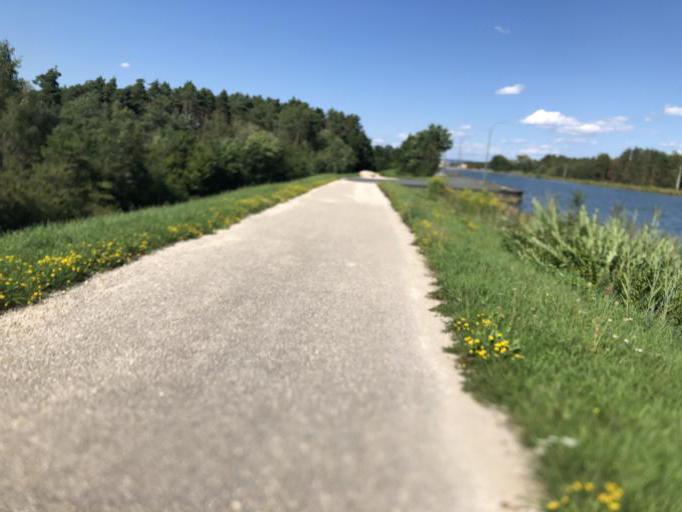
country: DE
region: Bavaria
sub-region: Regierungsbezirk Mittelfranken
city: Mohrendorf
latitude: 49.6186
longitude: 10.9758
